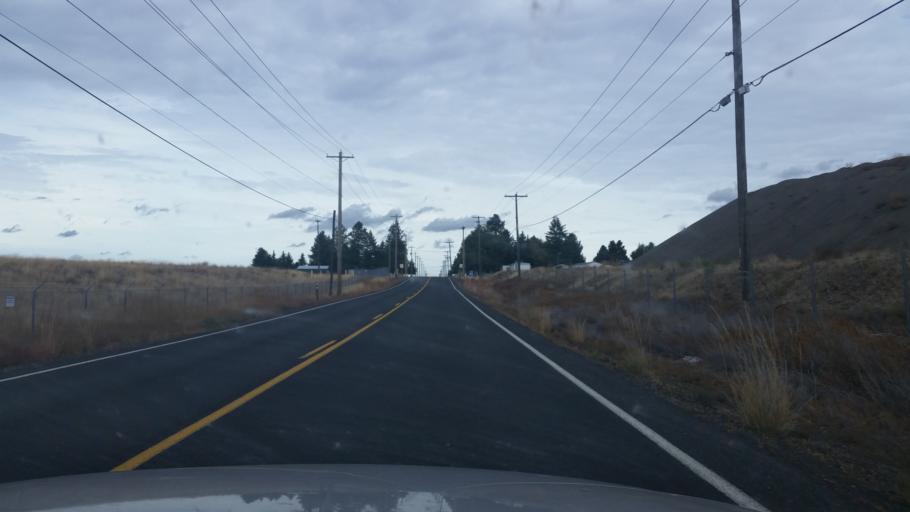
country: US
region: Washington
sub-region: Spokane County
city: Airway Heights
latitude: 47.6339
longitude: -117.6039
